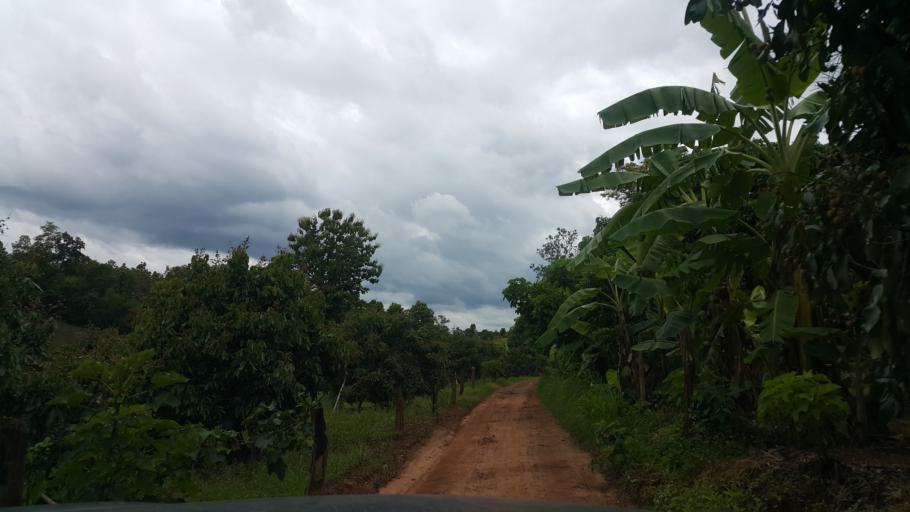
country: TH
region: Chiang Mai
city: Mae Taeng
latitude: 19.2302
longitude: 98.9993
